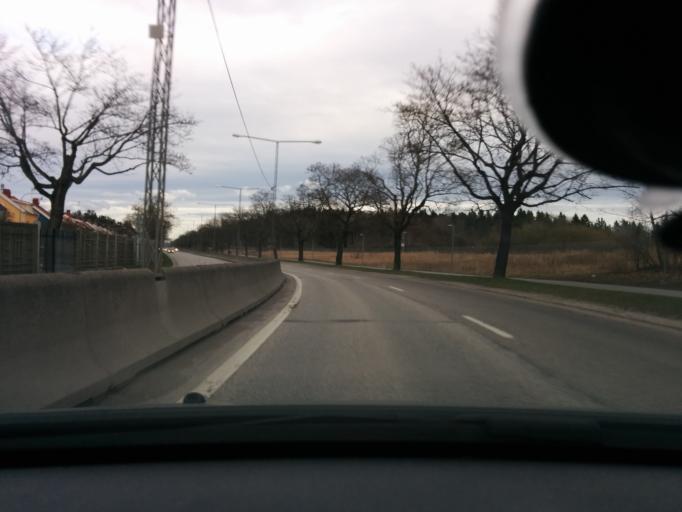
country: SE
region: Stockholm
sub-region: Stockholms Kommun
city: Bromma
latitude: 59.3421
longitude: 17.9088
